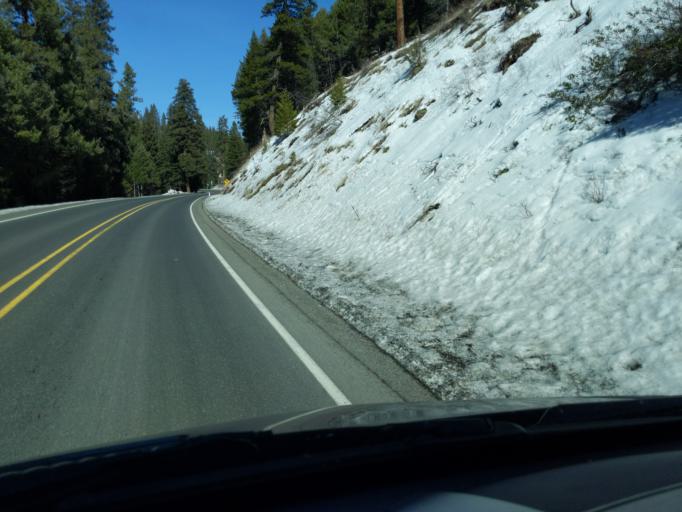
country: US
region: Oregon
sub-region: Grant County
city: John Day
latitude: 44.8865
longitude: -119.0131
